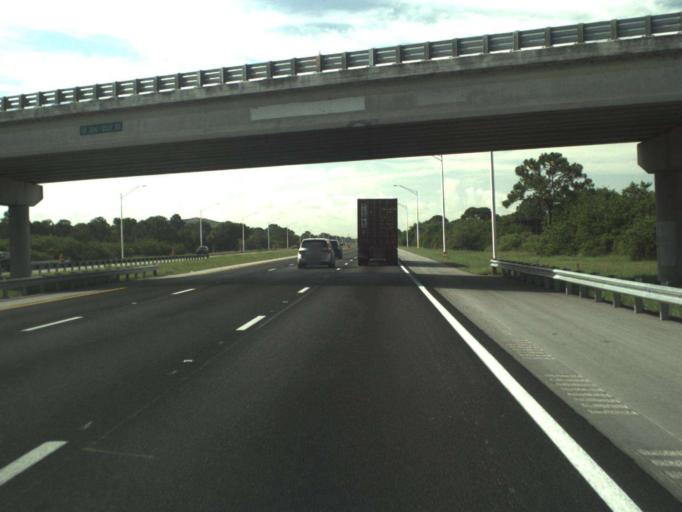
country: US
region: Florida
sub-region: Indian River County
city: West Vero Corridor
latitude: 27.5883
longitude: -80.5006
